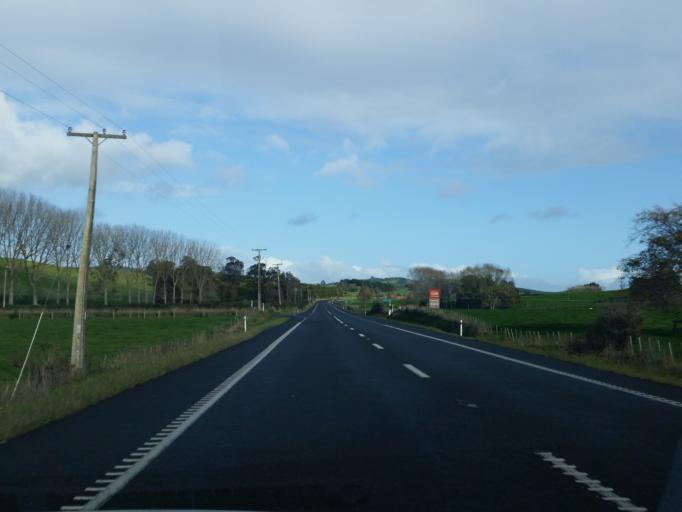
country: NZ
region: Waikato
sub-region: Hauraki District
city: Ngatea
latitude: -37.2866
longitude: 175.3913
